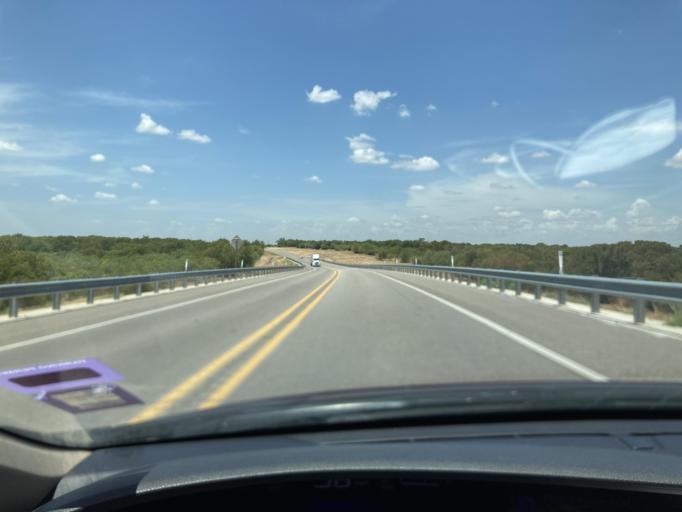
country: US
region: Texas
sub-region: Navarro County
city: Corsicana
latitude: 32.0472
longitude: -96.4732
